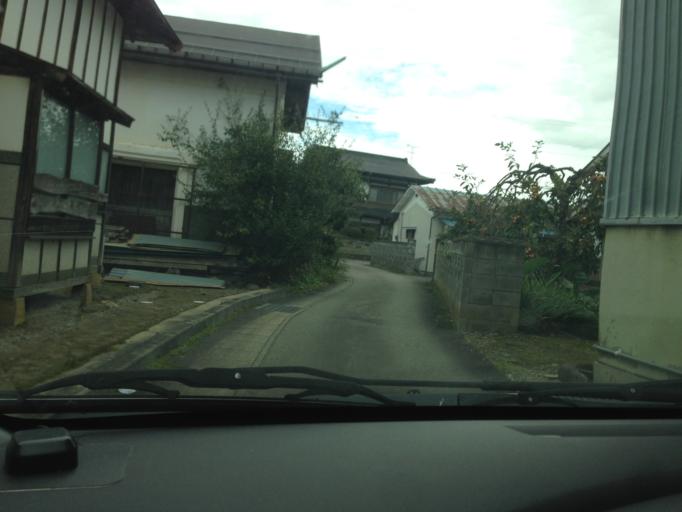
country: JP
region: Fukushima
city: Kitakata
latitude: 37.4724
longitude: 139.8539
